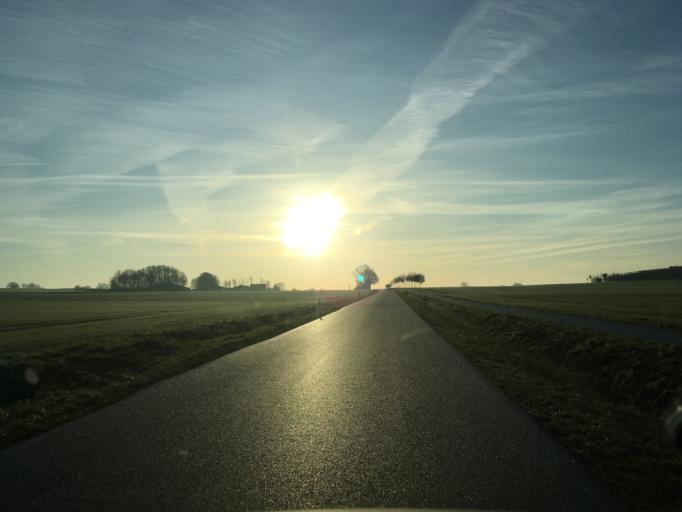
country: DE
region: North Rhine-Westphalia
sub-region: Regierungsbezirk Munster
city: Schoppingen
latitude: 52.0857
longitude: 7.2466
